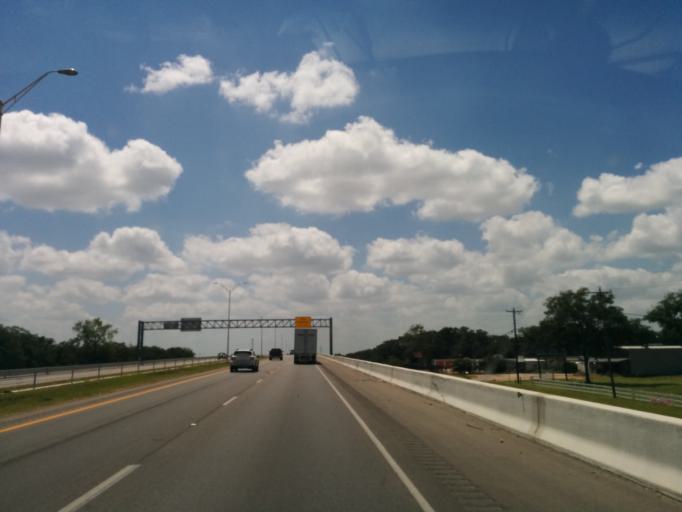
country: US
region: Texas
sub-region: Bastrop County
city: Bastrop
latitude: 30.1111
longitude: -97.3688
